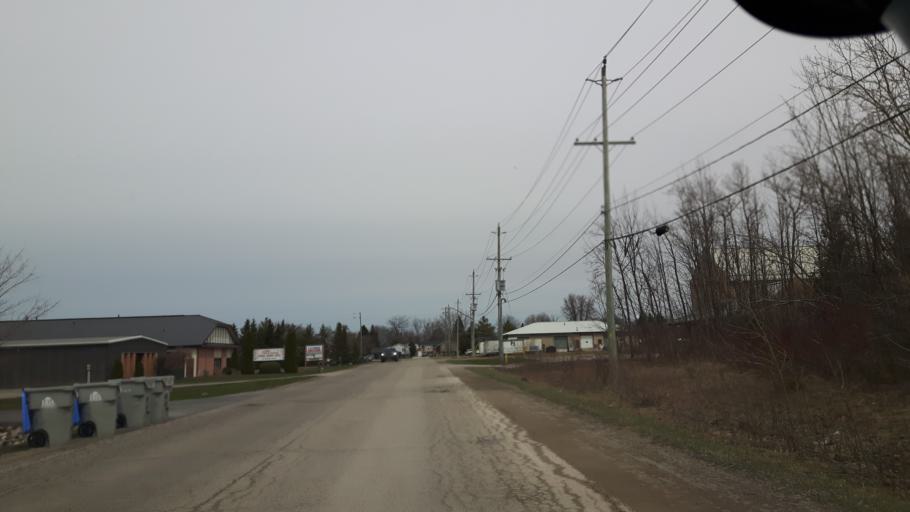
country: CA
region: Ontario
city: Goderich
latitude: 43.7293
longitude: -81.6994
